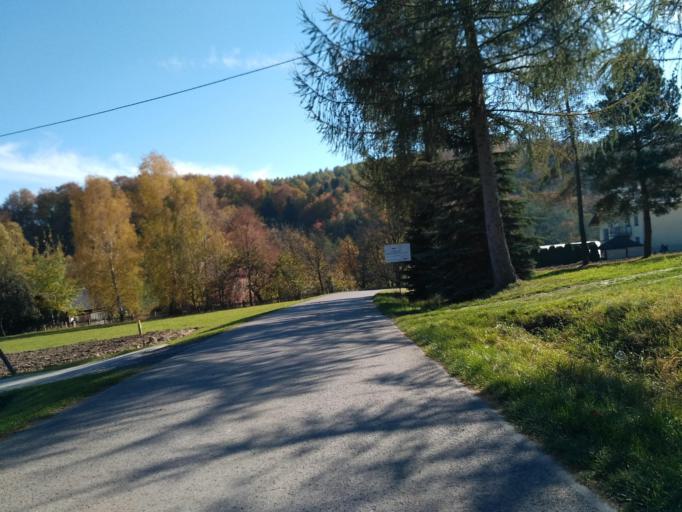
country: PL
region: Subcarpathian Voivodeship
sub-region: Powiat ropczycko-sedziszowski
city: Iwierzyce
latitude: 49.9779
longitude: 21.7285
